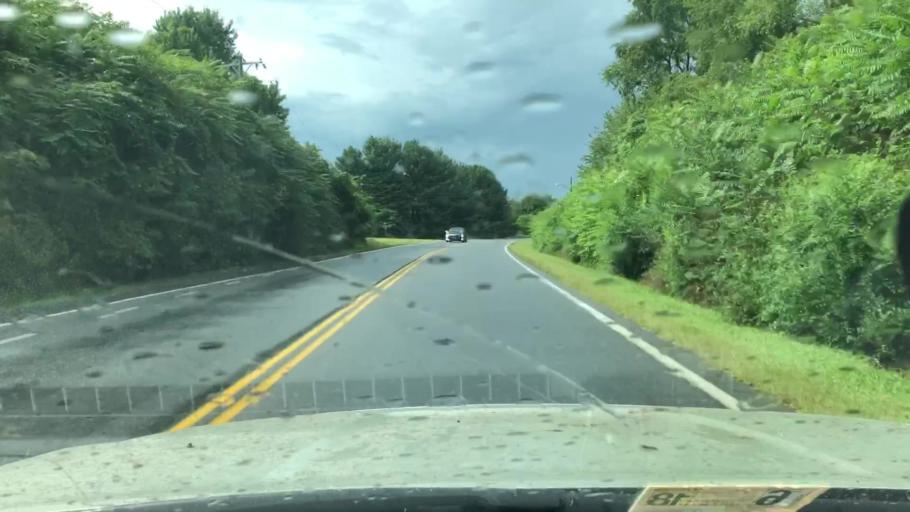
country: US
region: Virginia
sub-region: City of Waynesboro
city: Waynesboro
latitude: 38.0828
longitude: -78.8992
